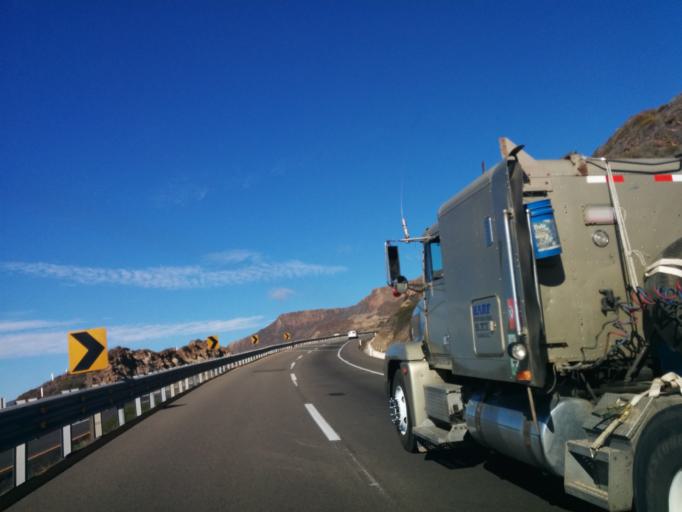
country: MX
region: Baja California
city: El Sauzal
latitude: 31.9154
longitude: -116.7534
